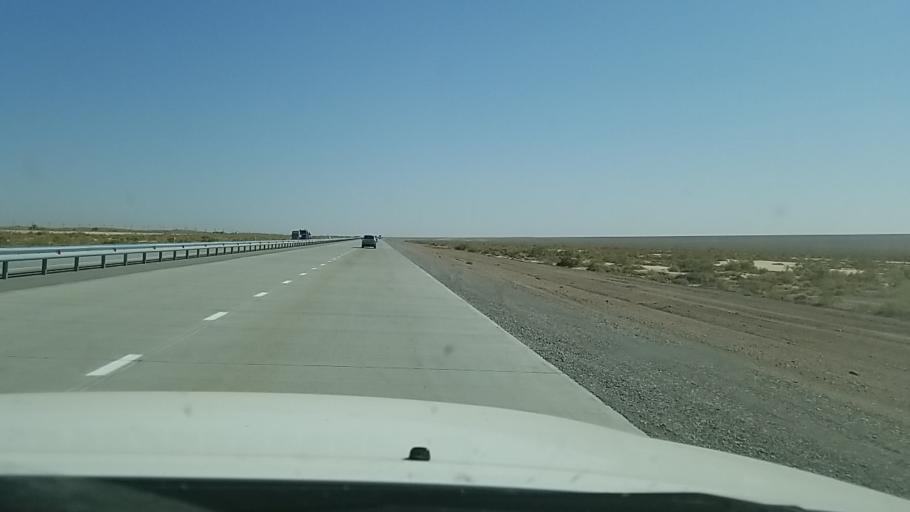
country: KZ
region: Almaty Oblysy
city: Kegen
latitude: 43.7532
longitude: 78.9089
